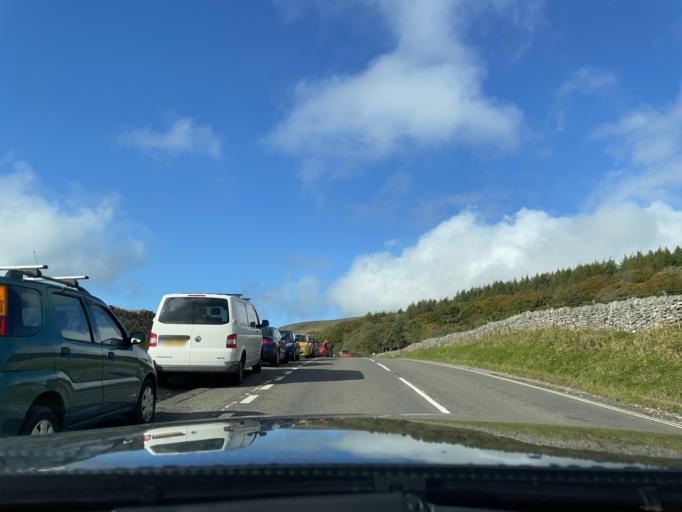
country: GB
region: England
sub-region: Derbyshire
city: High Peak
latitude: 53.3452
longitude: -1.8127
